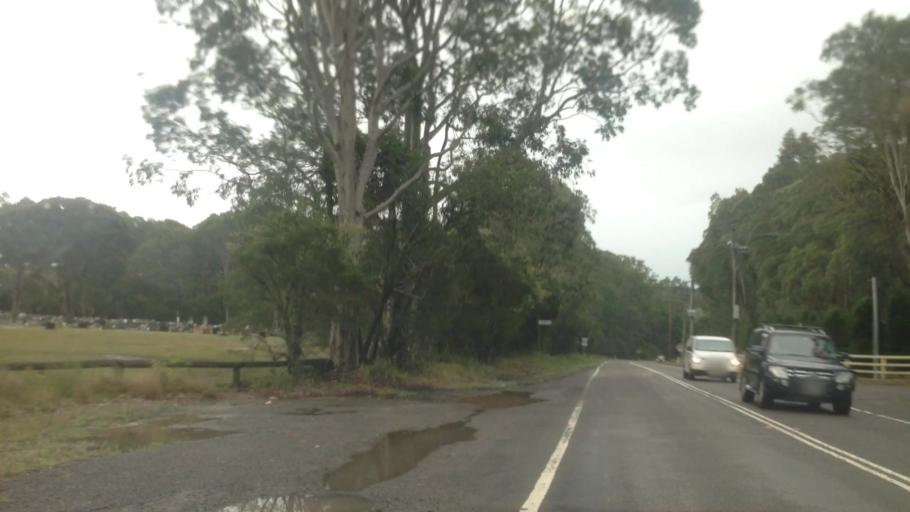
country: AU
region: New South Wales
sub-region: Wyong Shire
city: Little Jilliby
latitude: -33.2618
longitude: 151.3990
